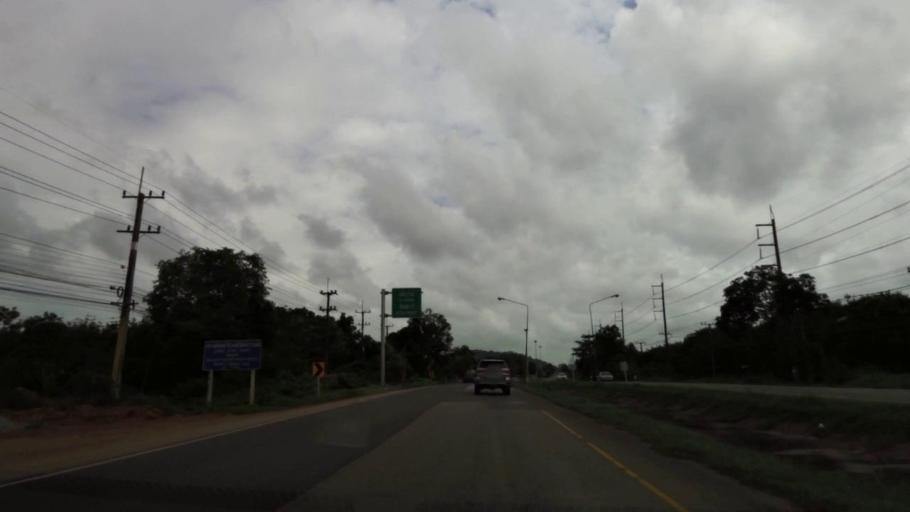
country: TH
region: Chanthaburi
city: Na Yai Am
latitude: 12.7341
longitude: 101.9026
